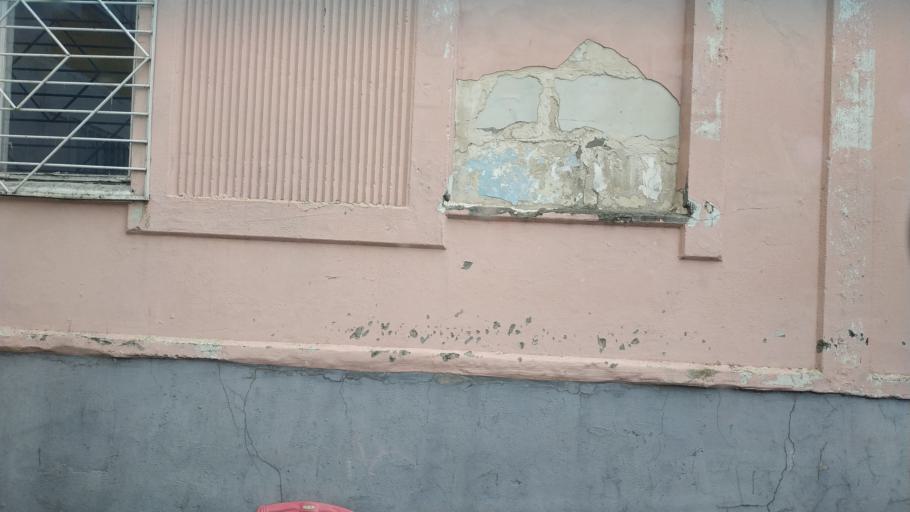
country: MD
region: Chisinau
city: Singera
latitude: 46.8872
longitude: 28.9941
